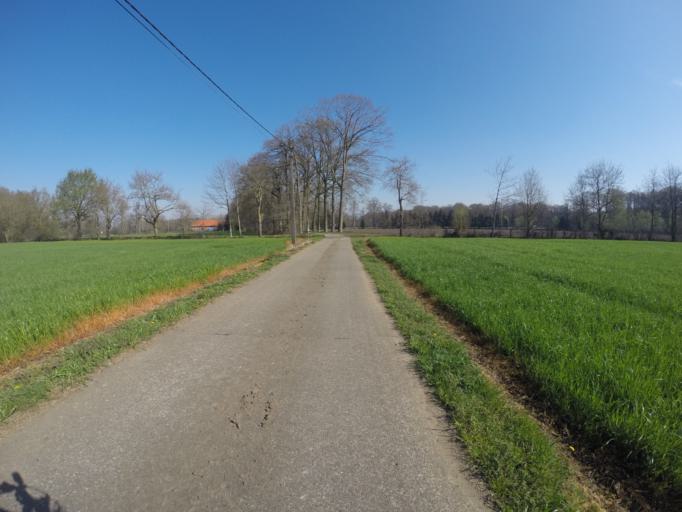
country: BE
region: Flanders
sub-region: Provincie West-Vlaanderen
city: Beernem
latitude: 51.1068
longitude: 3.3638
